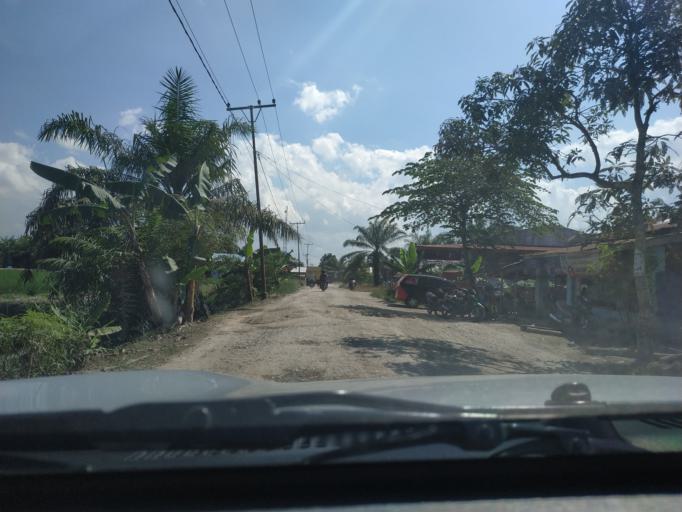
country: ID
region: North Sumatra
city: Tanjungbalai
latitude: 2.8774
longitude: 99.8612
